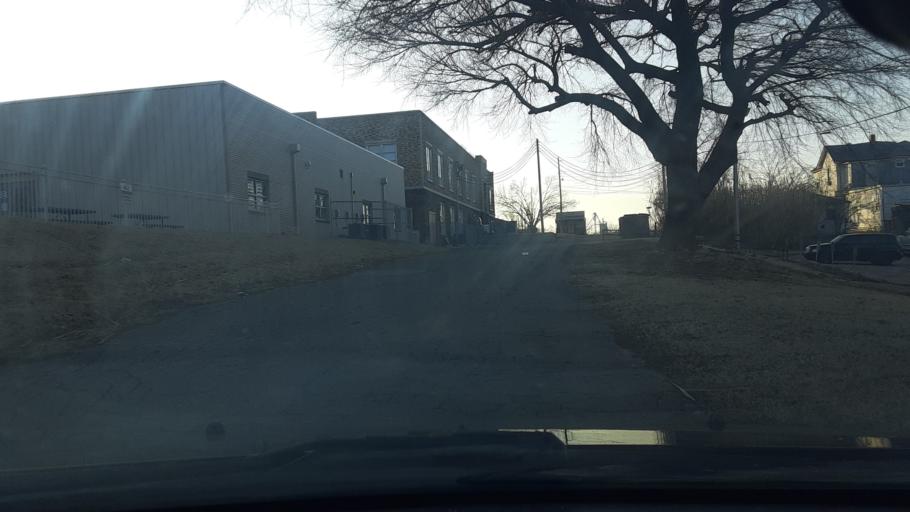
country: US
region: Oklahoma
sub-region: Logan County
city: Guthrie
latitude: 35.8874
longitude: -97.4229
